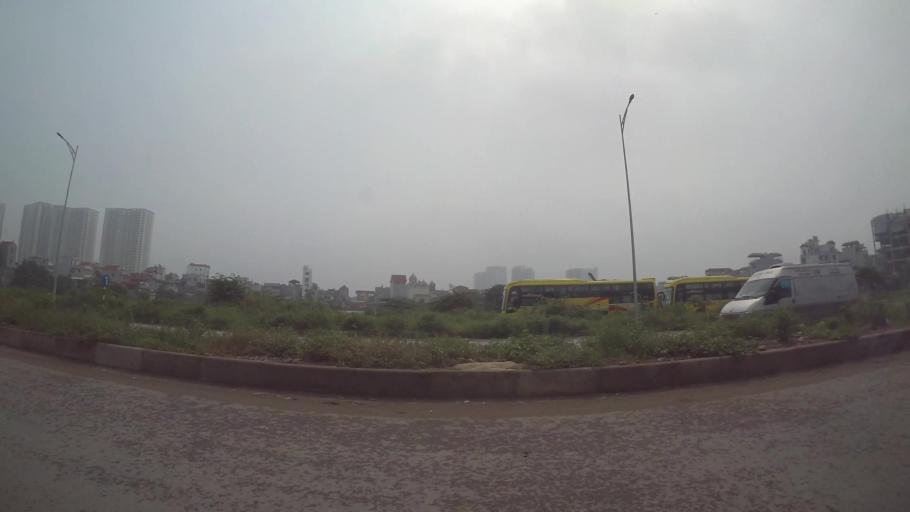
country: VN
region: Ha Noi
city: Van Dien
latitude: 20.9698
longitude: 105.8672
